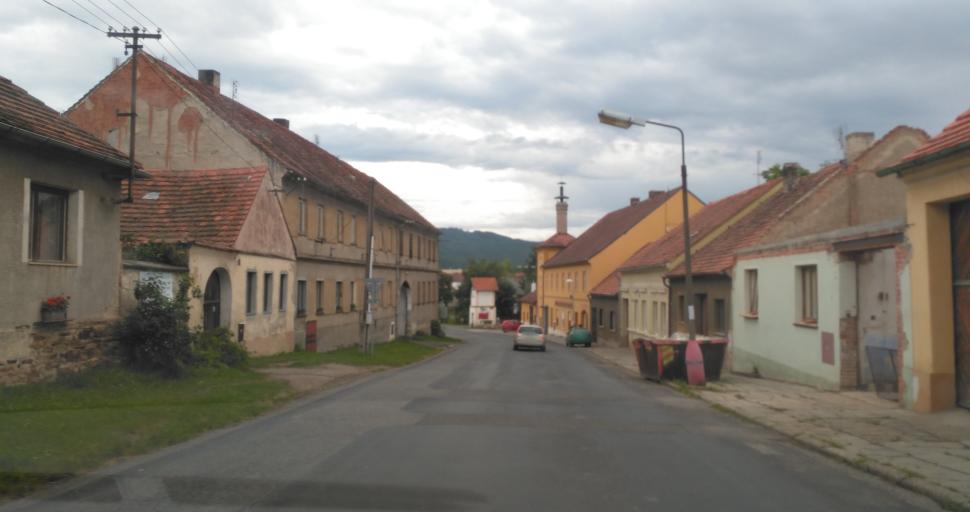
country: CZ
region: Central Bohemia
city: Hostomice
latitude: 49.8244
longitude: 14.0448
